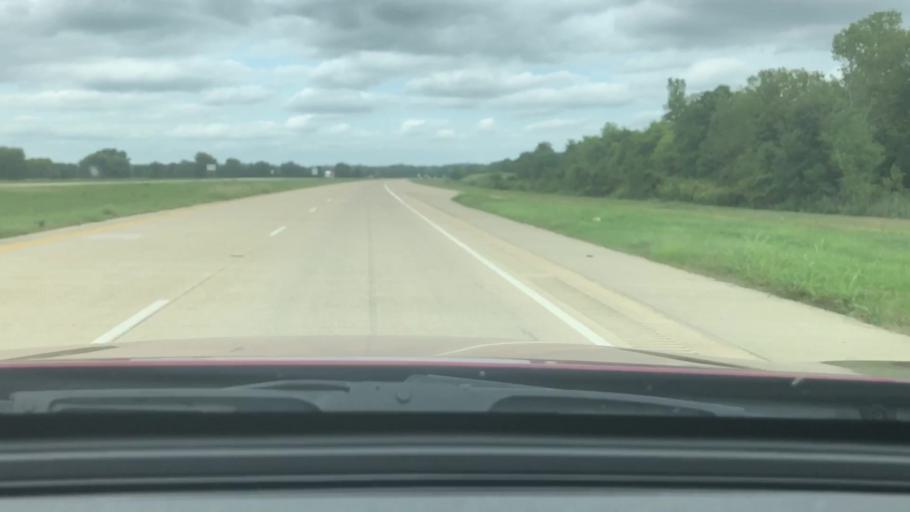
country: US
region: Louisiana
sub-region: Caddo Parish
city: Oil City
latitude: 32.7718
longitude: -93.8890
